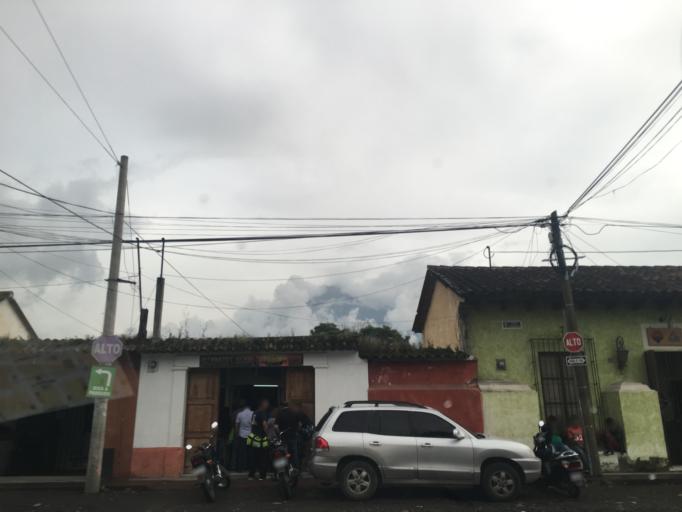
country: GT
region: Sacatepequez
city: Antigua Guatemala
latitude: 14.5563
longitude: -90.7411
